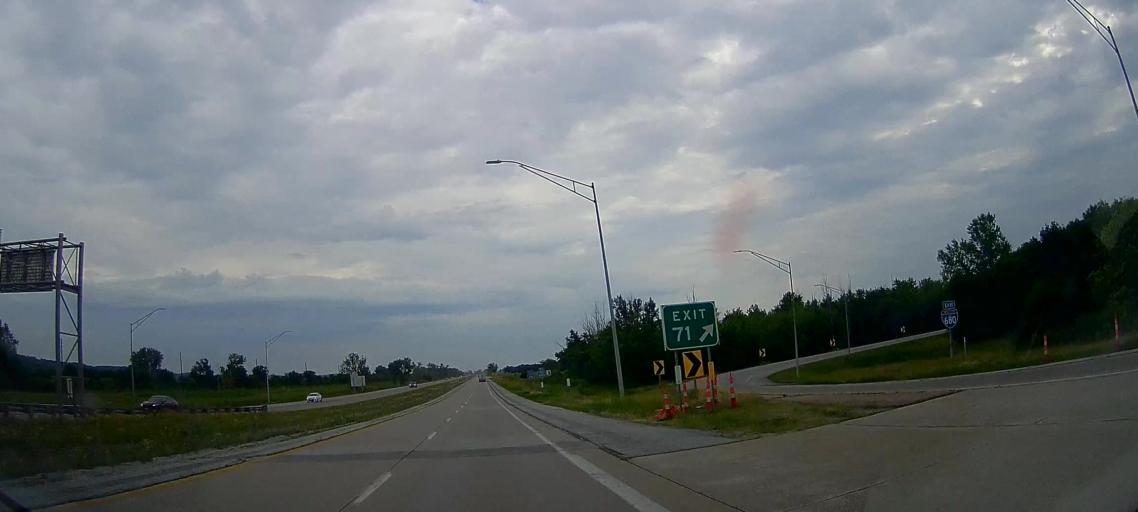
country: US
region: Iowa
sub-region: Harrison County
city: Missouri Valley
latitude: 41.4916
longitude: -95.9010
